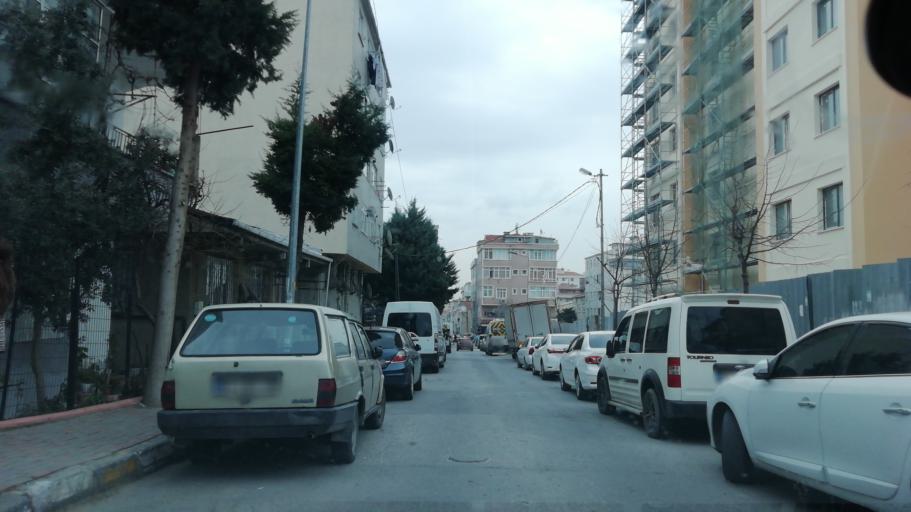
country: TR
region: Istanbul
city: Mahmutbey
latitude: 41.0248
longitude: 28.8293
